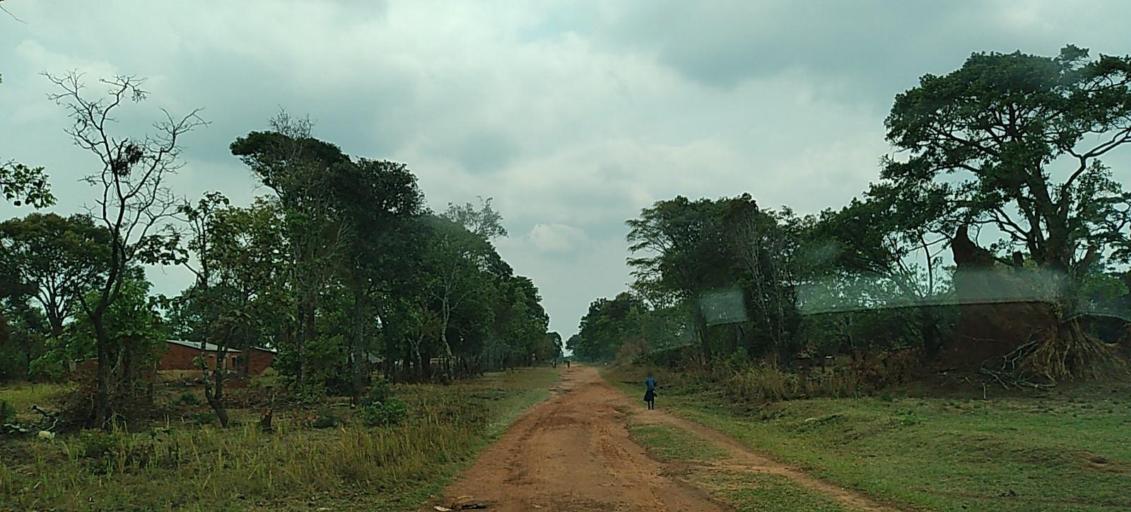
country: ZM
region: North-Western
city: Mwinilunga
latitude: -11.5292
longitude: 24.7855
